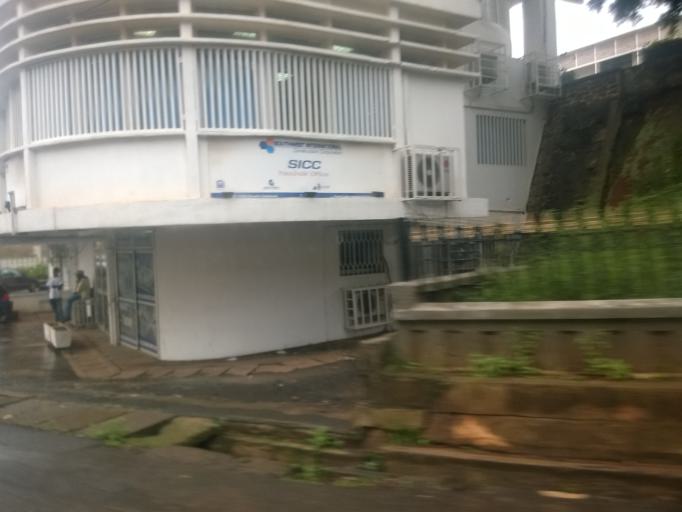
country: CM
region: Centre
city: Yaounde
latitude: 3.8696
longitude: 11.5168
